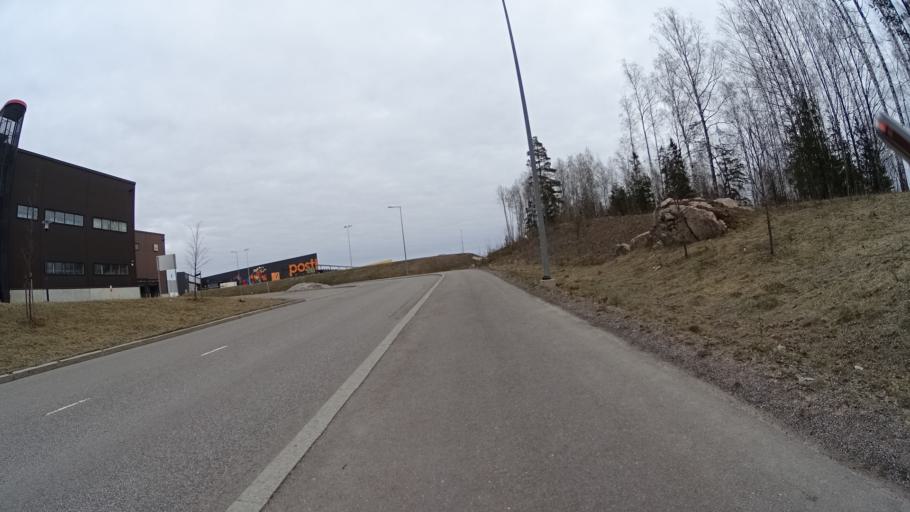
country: FI
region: Uusimaa
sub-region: Helsinki
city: Teekkarikylae
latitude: 60.3016
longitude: 24.8950
